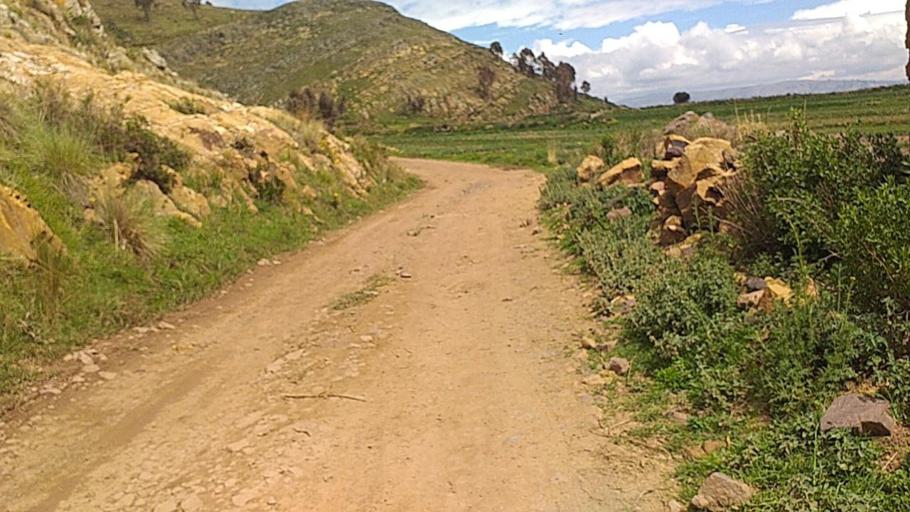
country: BO
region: La Paz
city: Batallas
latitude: -16.3374
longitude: -68.6365
